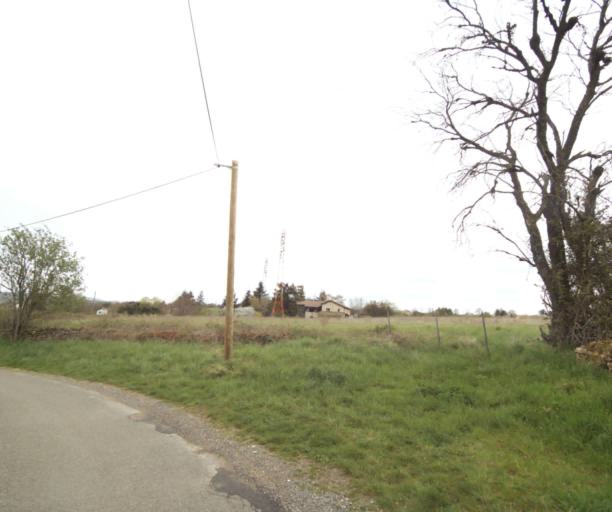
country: FR
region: Bourgogne
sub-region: Departement de Saone-et-Loire
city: Charnay-les-Macon
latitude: 46.3196
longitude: 4.7846
